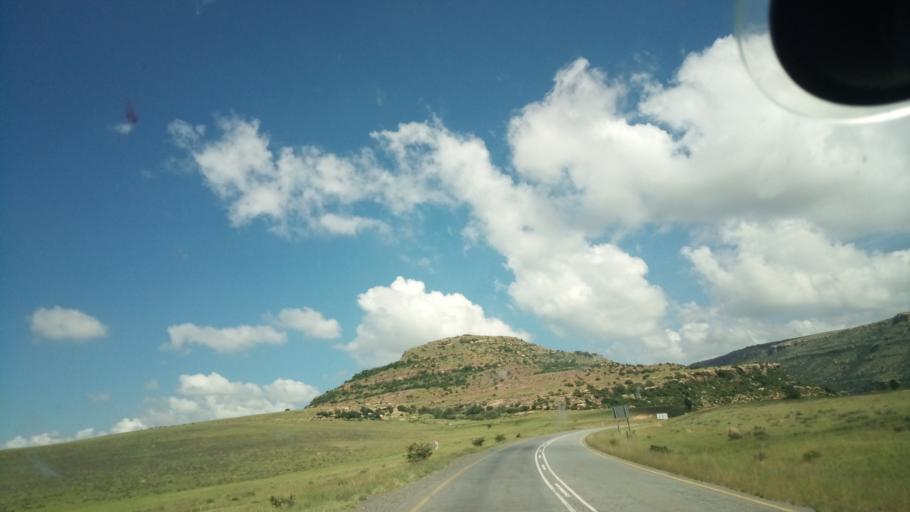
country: ZA
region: Orange Free State
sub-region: Thabo Mofutsanyana District Municipality
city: Ficksburg
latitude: -28.8935
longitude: 27.8474
